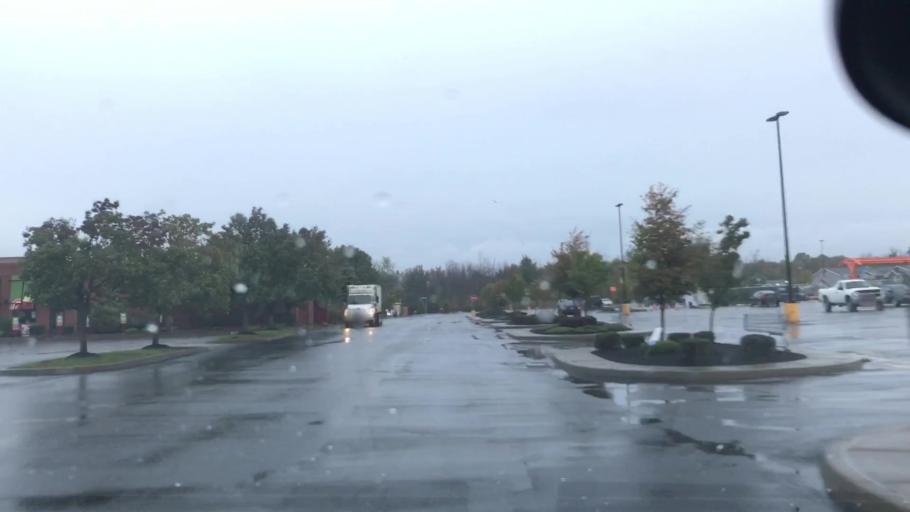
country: US
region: New York
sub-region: Erie County
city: Depew
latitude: 42.8815
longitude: -78.6958
